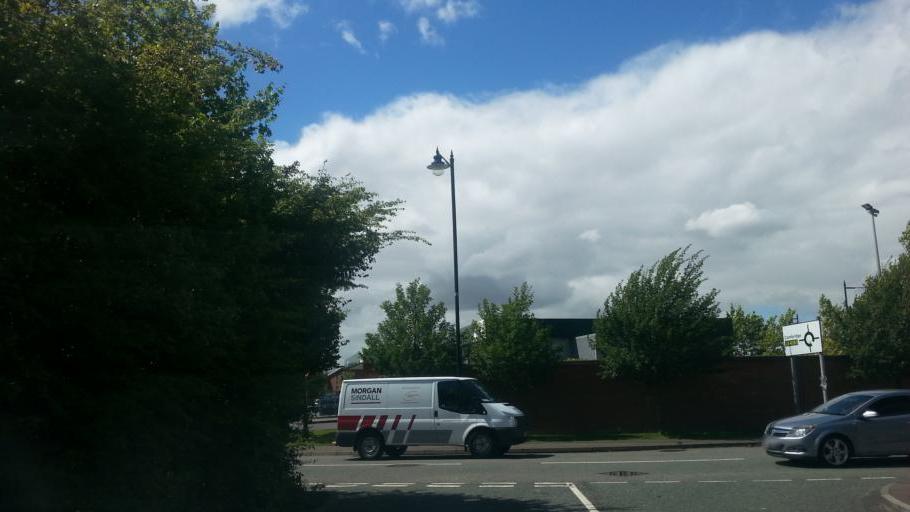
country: GB
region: England
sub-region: Cambridgeshire
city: Papworth Everard
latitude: 52.2198
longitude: -0.0669
